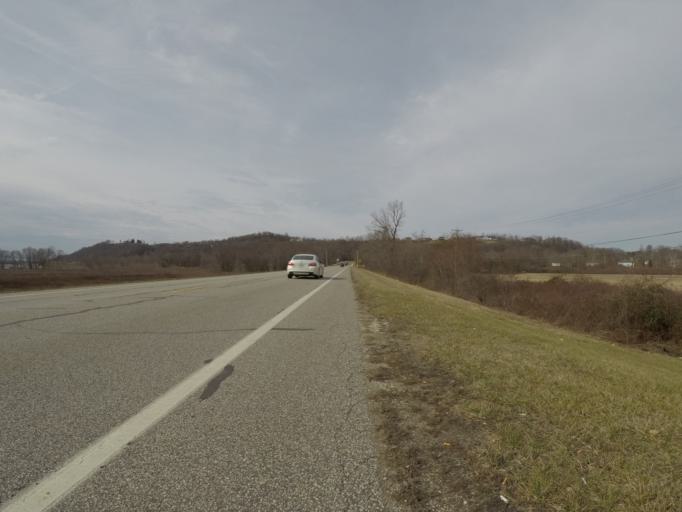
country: US
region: West Virginia
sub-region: Cabell County
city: Huntington
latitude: 38.4413
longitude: -82.3946
